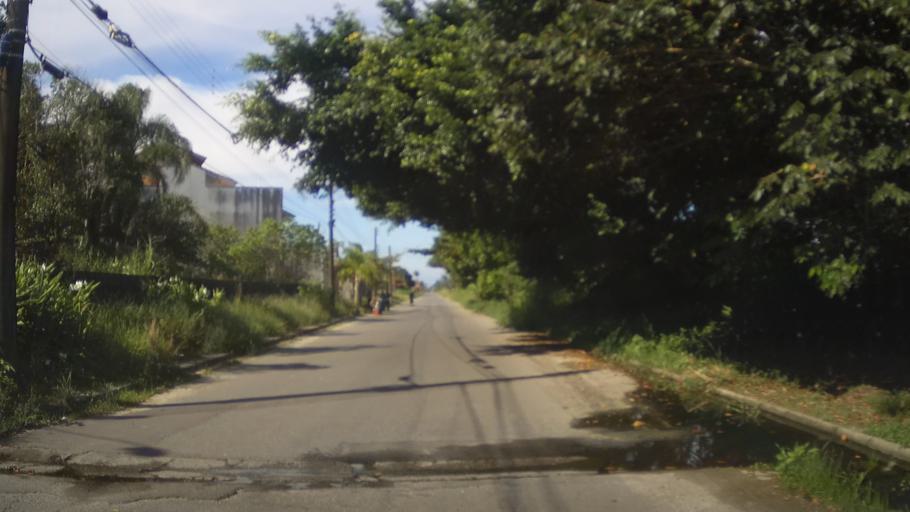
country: BR
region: Sao Paulo
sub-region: Itanhaem
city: Itanhaem
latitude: -24.2164
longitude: -46.8555
